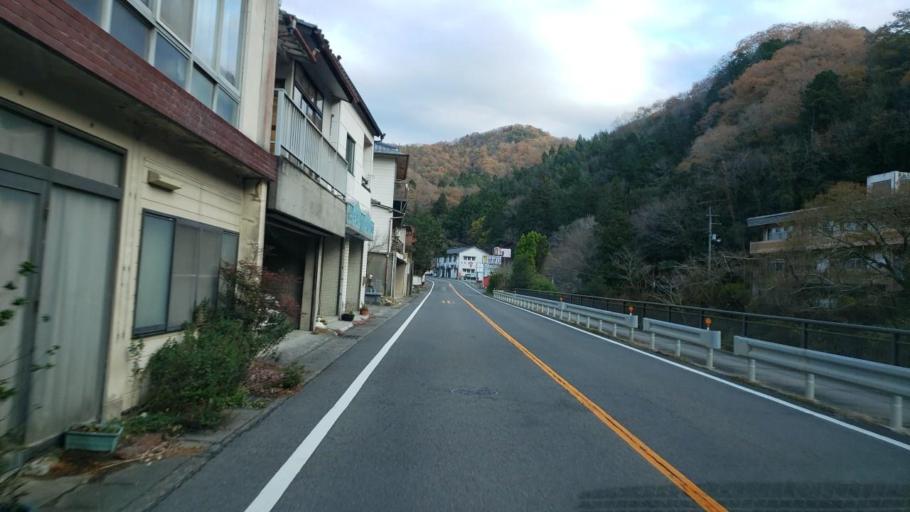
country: JP
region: Tokushima
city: Wakimachi
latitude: 34.1690
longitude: 134.0844
